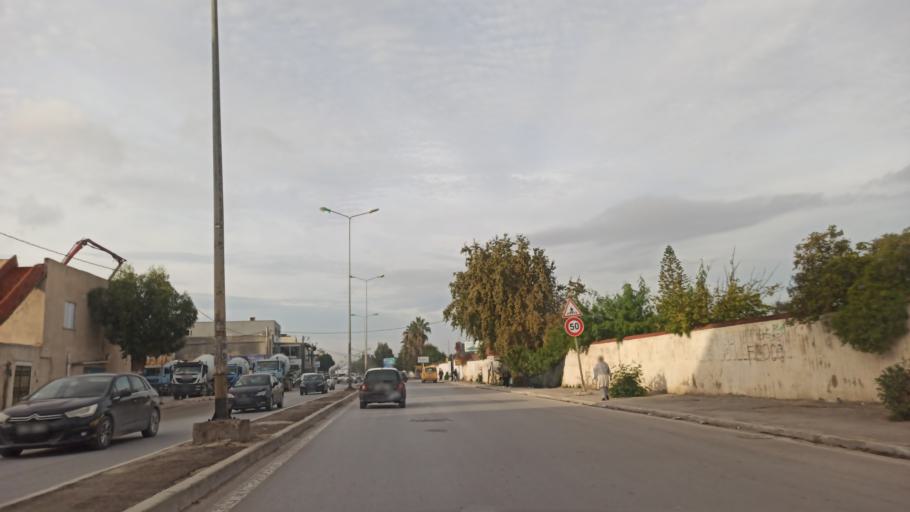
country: TN
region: Ariana
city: Ariana
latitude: 36.8740
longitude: 10.2386
